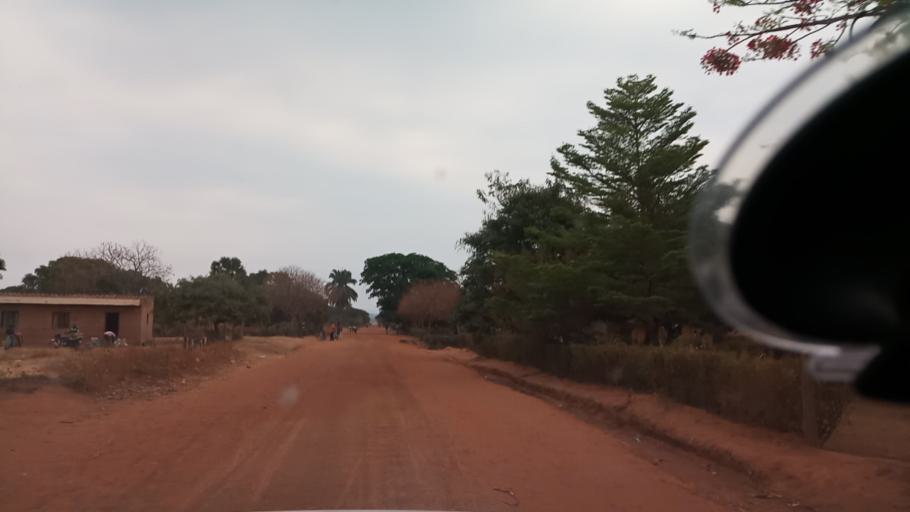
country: ZM
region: Luapula
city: Nchelenge
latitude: -9.2769
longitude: 28.3274
